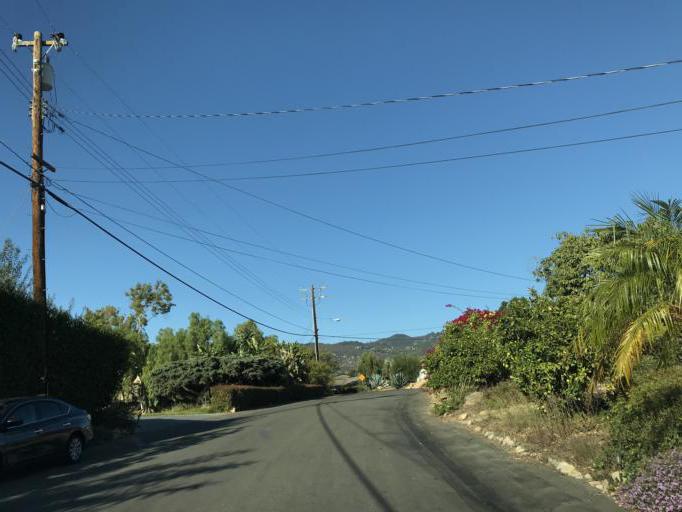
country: US
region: California
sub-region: Santa Barbara County
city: Goleta
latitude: 34.4619
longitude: -119.8212
